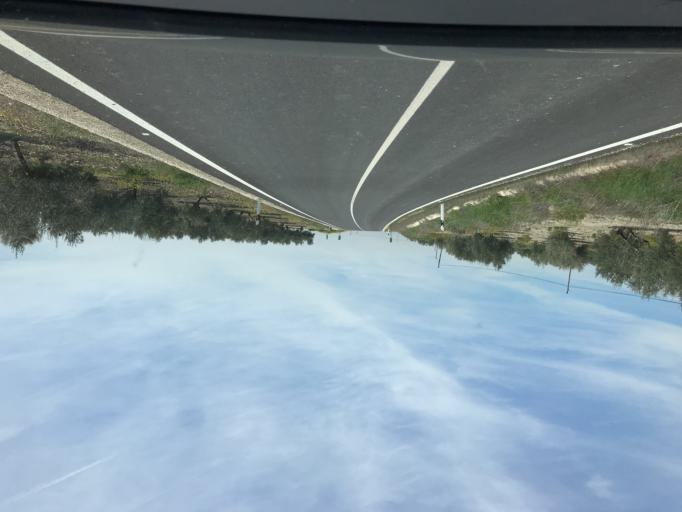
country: ES
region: Andalusia
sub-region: Provincia de Jaen
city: Higuera de Calatrava
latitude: 37.8009
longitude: -4.1506
